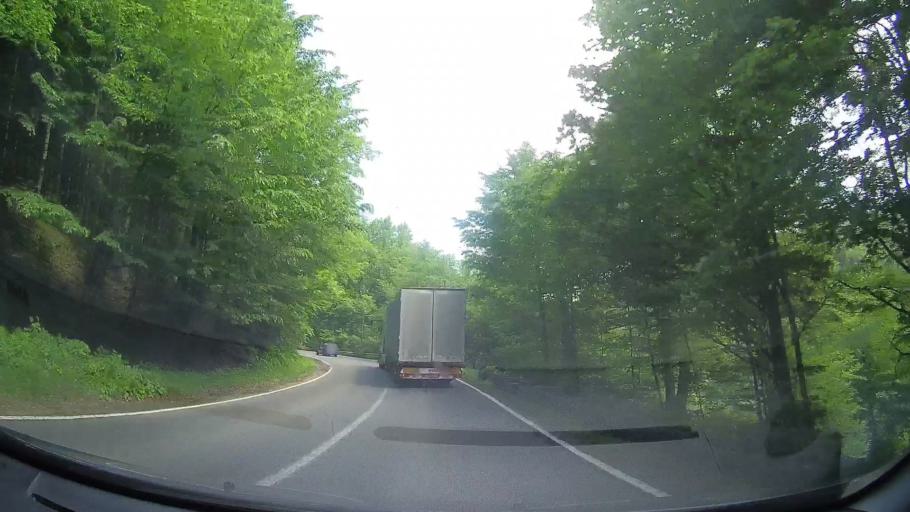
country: RO
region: Prahova
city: Maneciu
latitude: 45.3742
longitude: 25.9295
